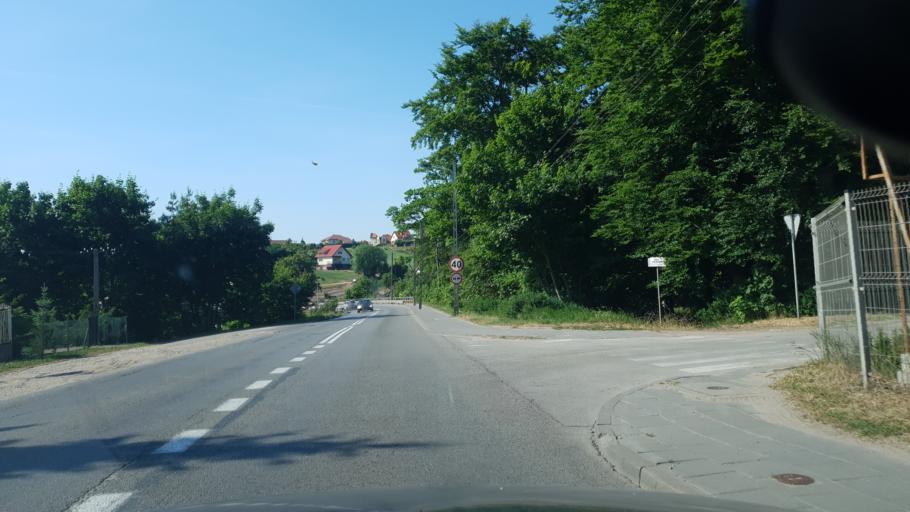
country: PL
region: Pomeranian Voivodeship
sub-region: Gdynia
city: Wielki Kack
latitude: 54.4368
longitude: 18.4631
